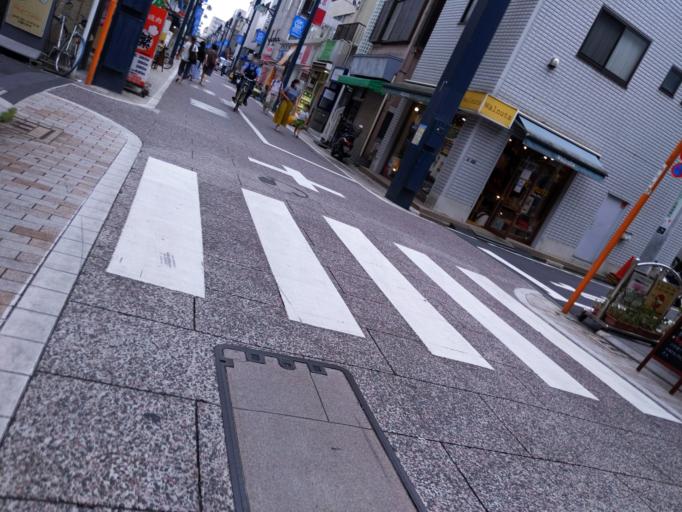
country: JP
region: Tokyo
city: Tokyo
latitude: 35.6151
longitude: 139.7178
